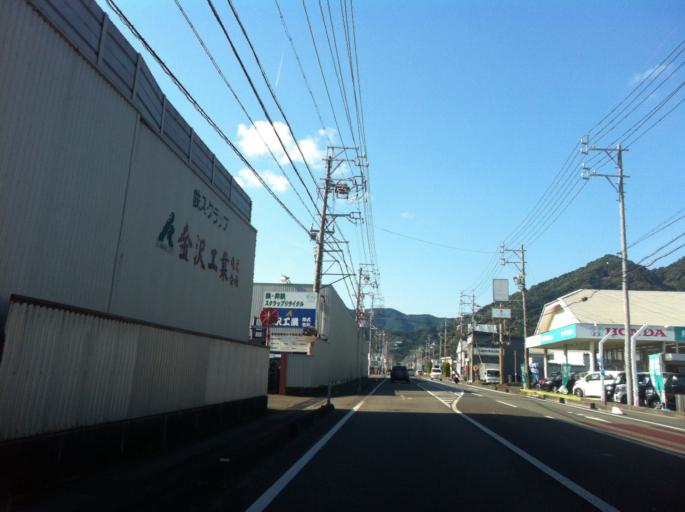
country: JP
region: Shizuoka
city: Shizuoka-shi
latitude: 34.9483
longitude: 138.3516
